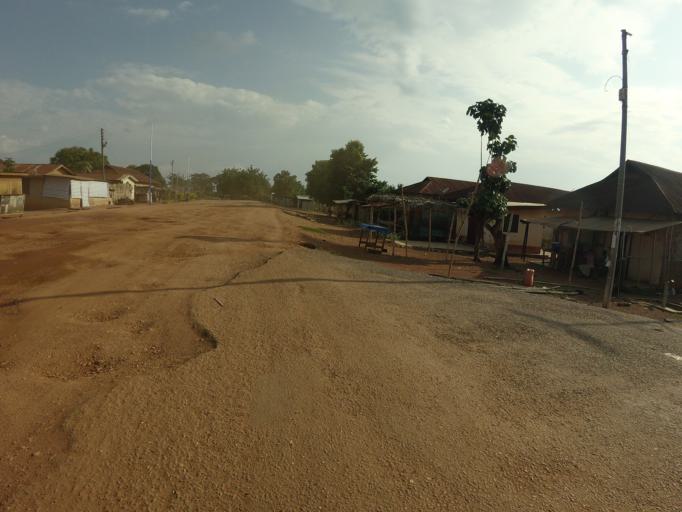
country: GH
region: Volta
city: Hohoe
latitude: 7.1233
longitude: 0.4592
